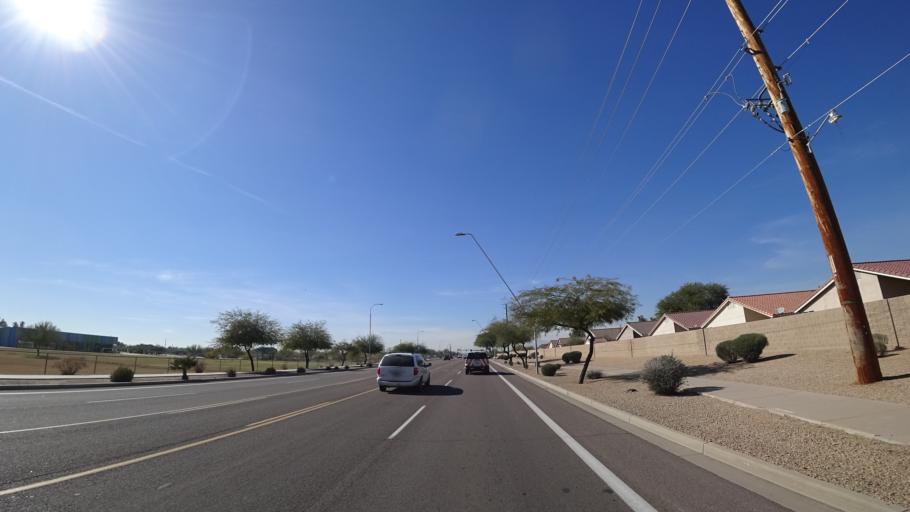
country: US
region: Arizona
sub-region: Maricopa County
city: Tolleson
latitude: 33.5083
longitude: -112.2861
